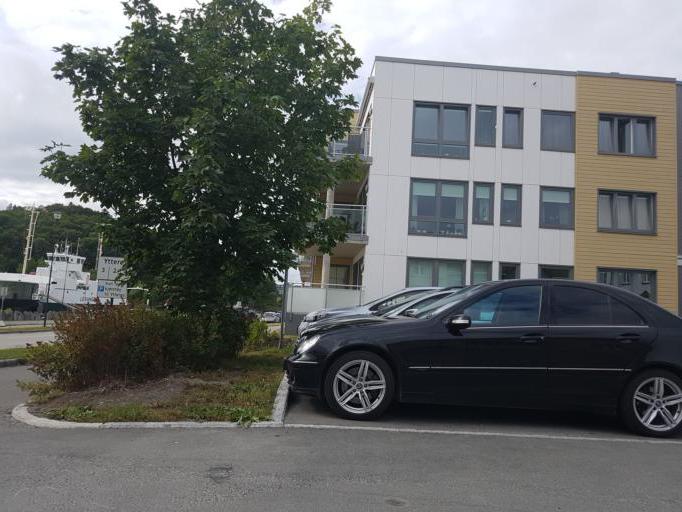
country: NO
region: Nord-Trondelag
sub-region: Levanger
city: Levanger
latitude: 63.7488
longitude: 11.3011
